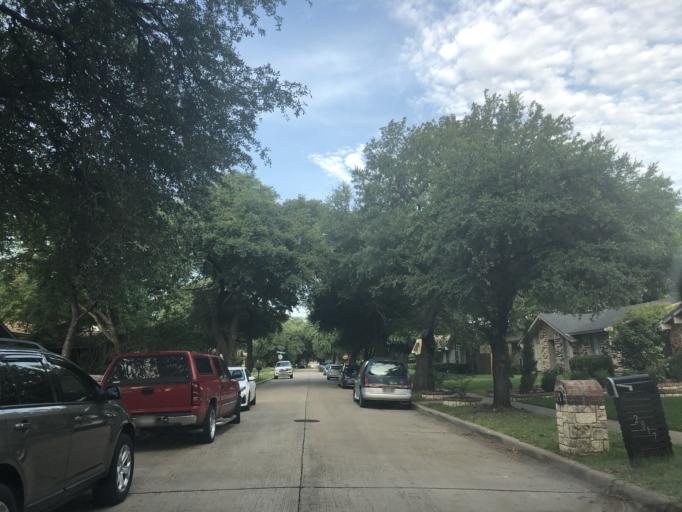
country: US
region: Texas
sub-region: Dallas County
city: Sunnyvale
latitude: 32.8398
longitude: -96.5855
